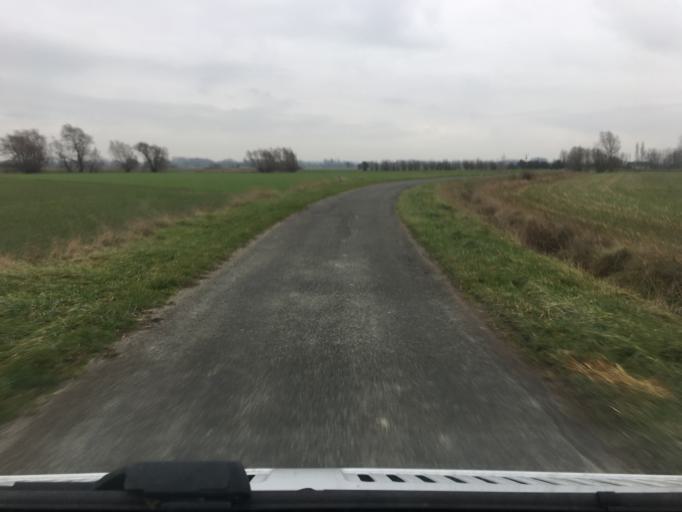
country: FR
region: Picardie
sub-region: Departement de la Somme
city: Pende
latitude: 50.1892
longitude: 1.5482
